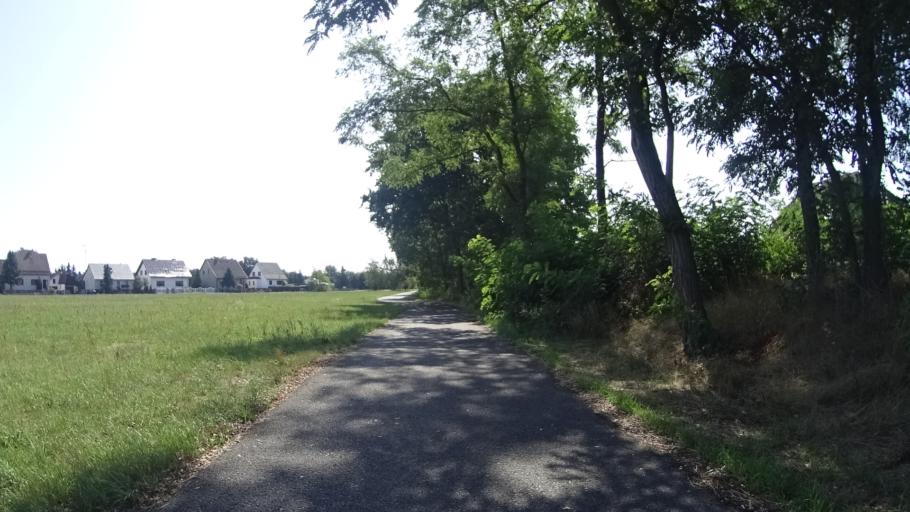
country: DE
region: Brandenburg
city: Cottbus
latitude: 51.7937
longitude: 14.3013
